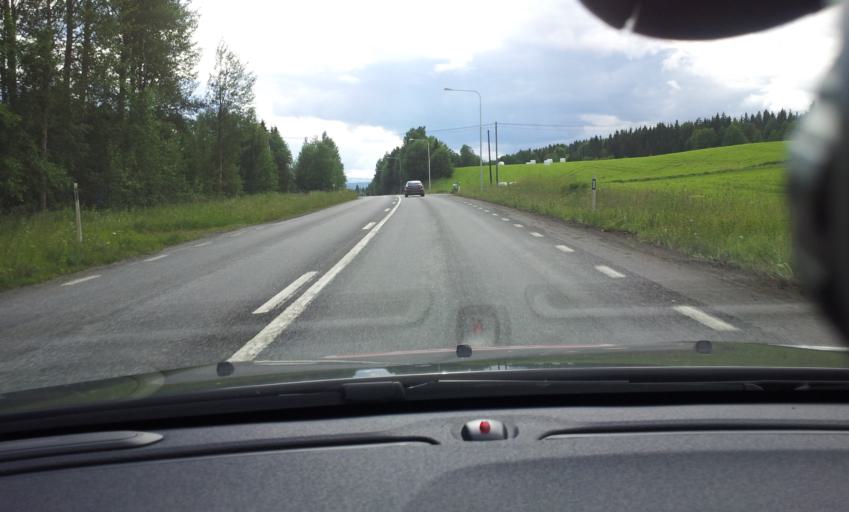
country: SE
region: Jaemtland
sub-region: Are Kommun
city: Jarpen
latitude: 63.3343
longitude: 13.4179
